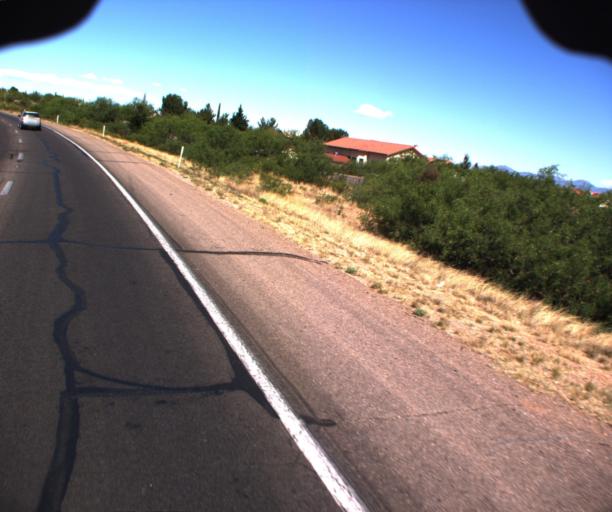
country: US
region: Arizona
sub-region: Cochise County
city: Sierra Vista
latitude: 31.5694
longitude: -110.2607
